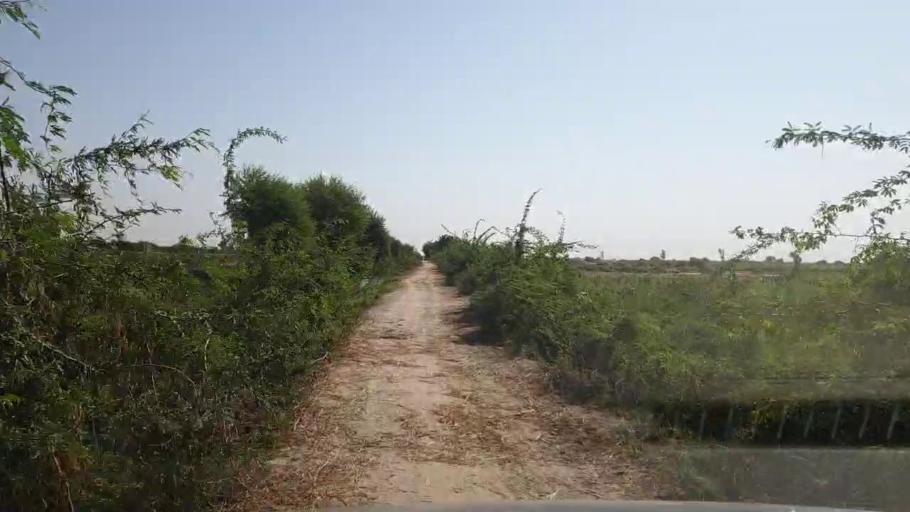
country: PK
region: Sindh
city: Kadhan
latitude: 24.6183
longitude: 68.9968
